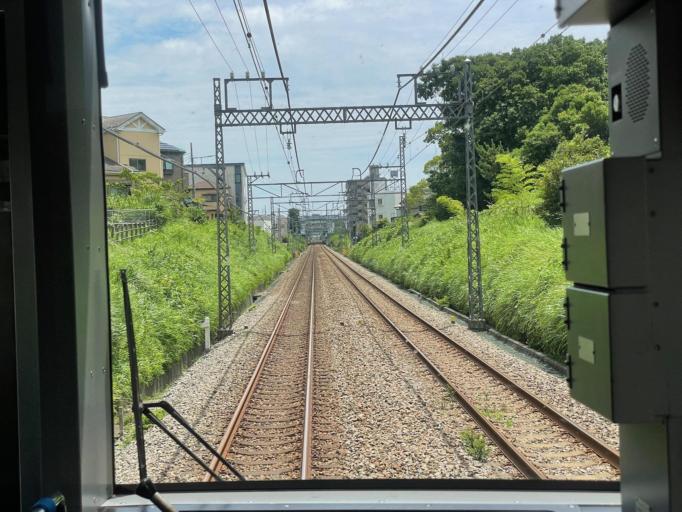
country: JP
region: Kanagawa
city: Fujisawa
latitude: 35.3882
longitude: 139.4693
